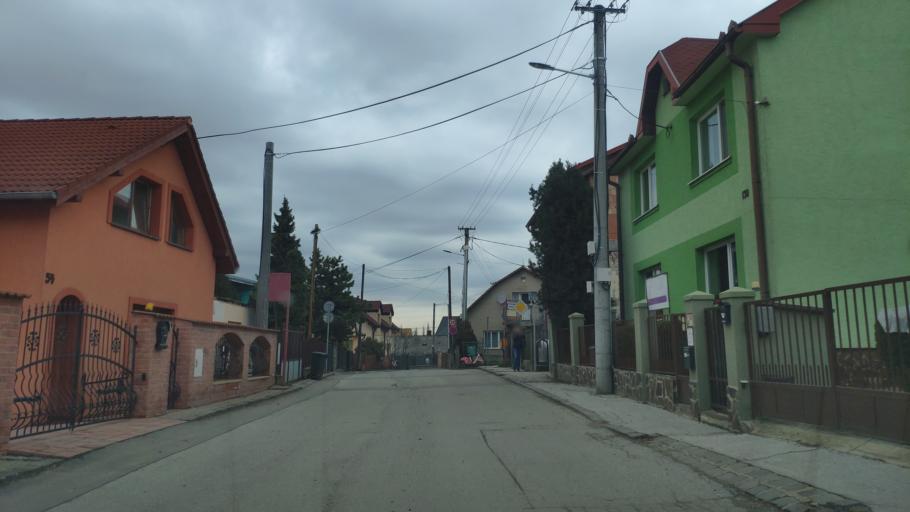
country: SK
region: Kosicky
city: Kosice
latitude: 48.6998
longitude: 21.2841
